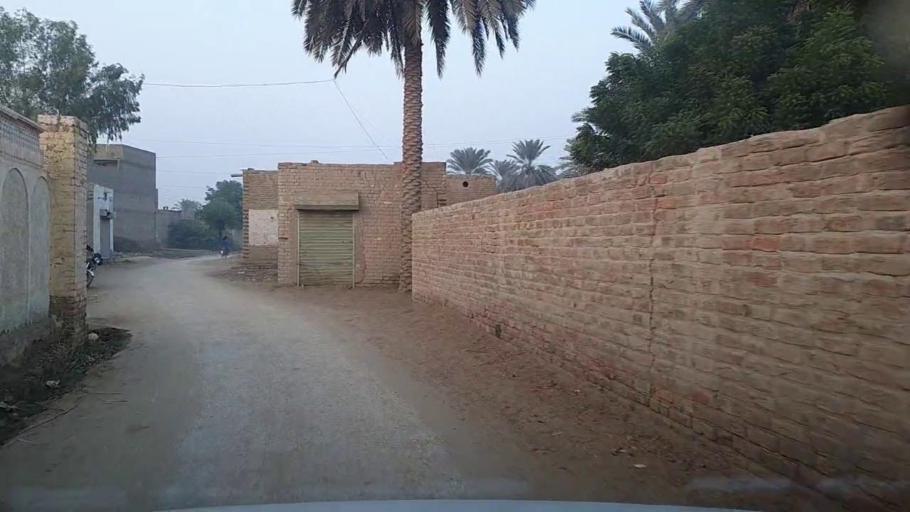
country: PK
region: Sindh
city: Bozdar
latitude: 27.0696
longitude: 68.5981
